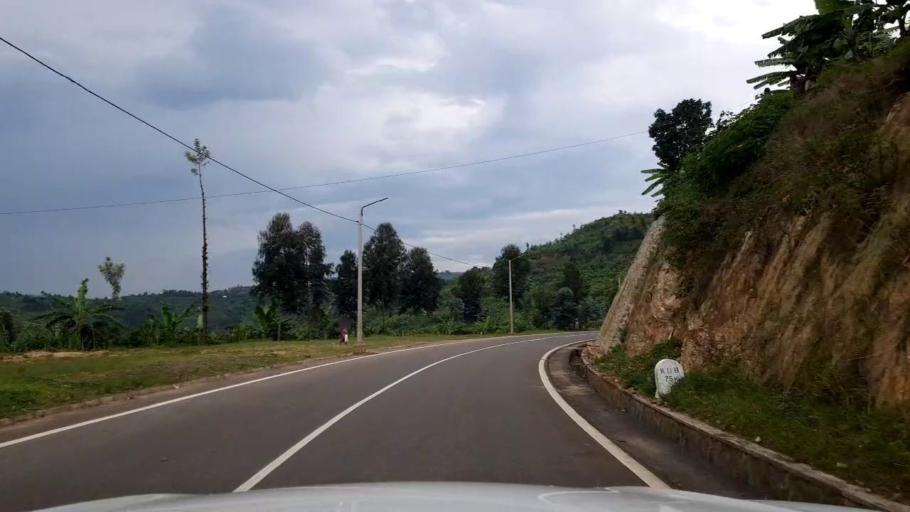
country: RW
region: Western Province
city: Kibuye
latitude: -2.0235
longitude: 29.3878
